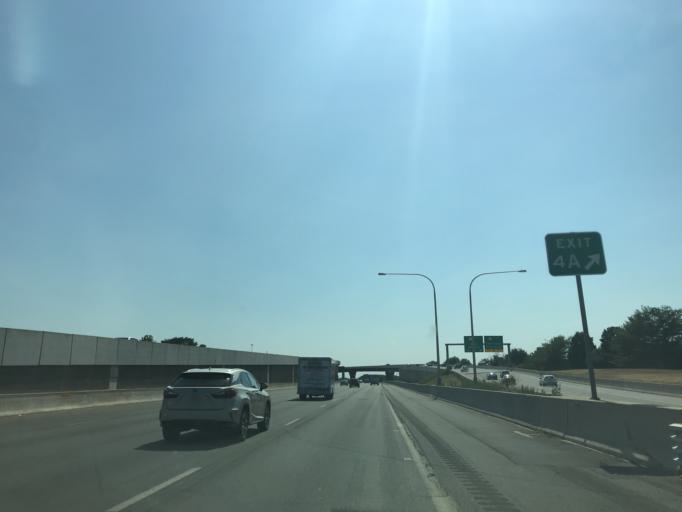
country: US
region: Delaware
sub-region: New Castle County
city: Newport
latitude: 39.6864
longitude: -75.6491
